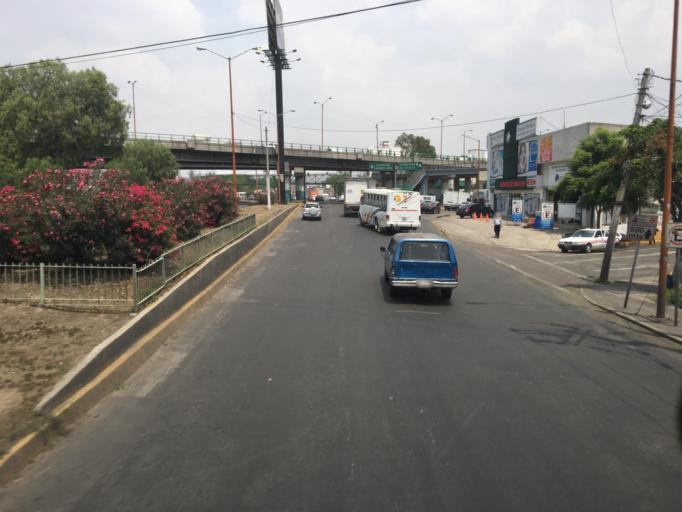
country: MX
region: Mexico
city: Tlalnepantla
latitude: 19.5327
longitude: -99.1796
